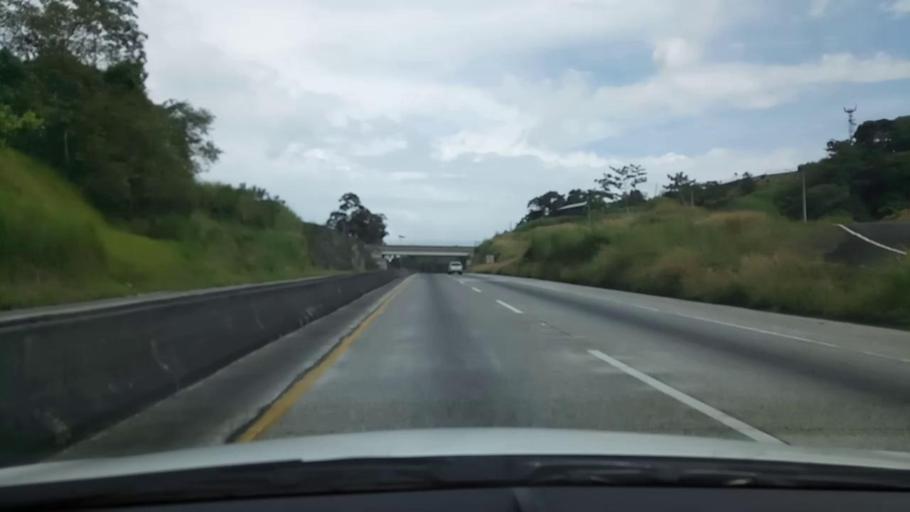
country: PA
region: Colon
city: Gatun
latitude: 9.2839
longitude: -79.7392
